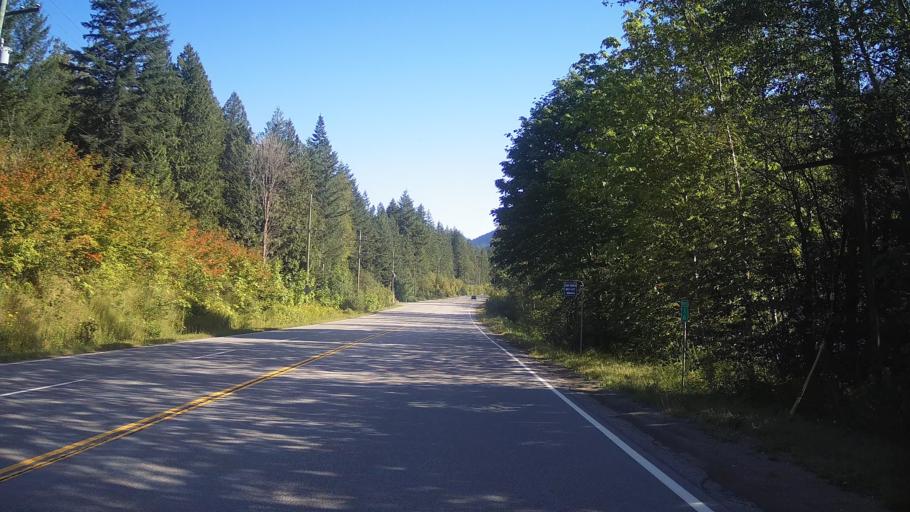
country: CA
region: British Columbia
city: Hope
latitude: 49.4998
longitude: -121.4200
